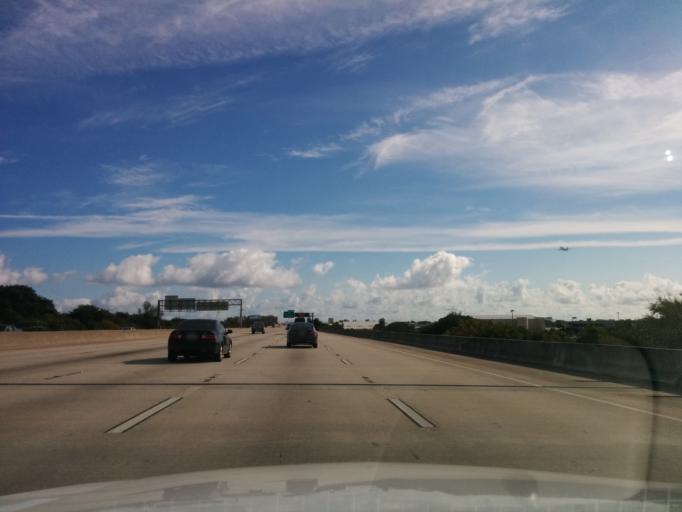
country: US
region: Florida
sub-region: Broward County
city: Dania Beach
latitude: 26.0812
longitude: -80.1511
